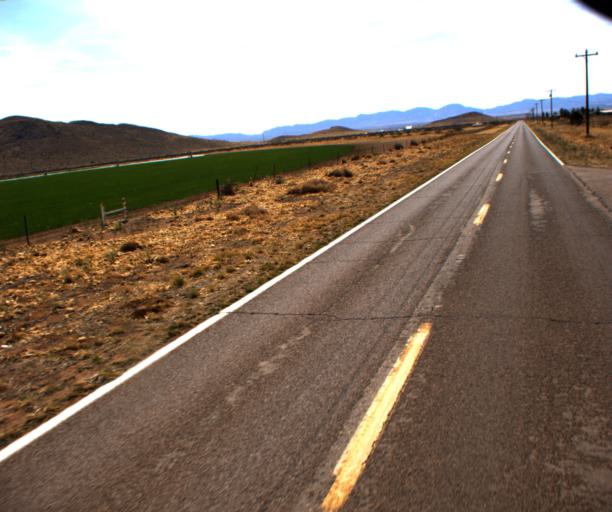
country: US
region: Arizona
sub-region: Cochise County
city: Willcox
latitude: 31.8765
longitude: -109.6481
